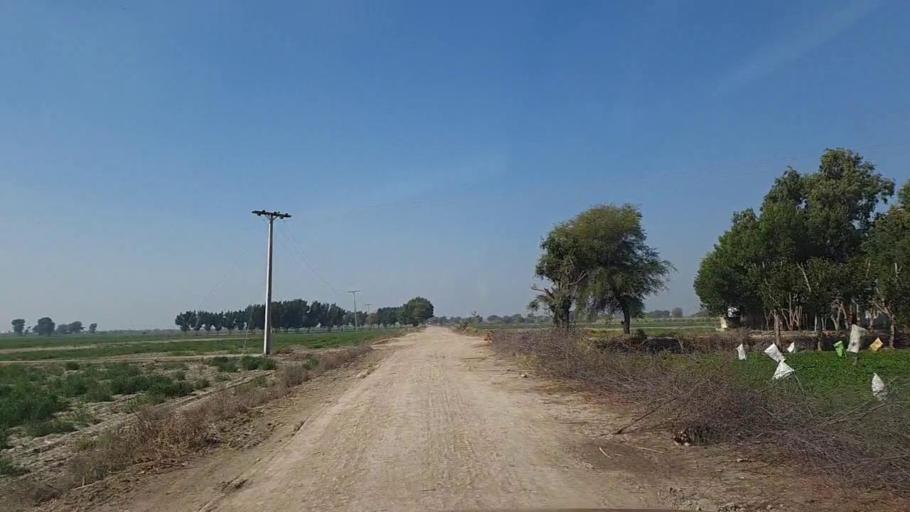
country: PK
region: Sindh
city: Nawabshah
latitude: 26.2823
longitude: 68.3807
